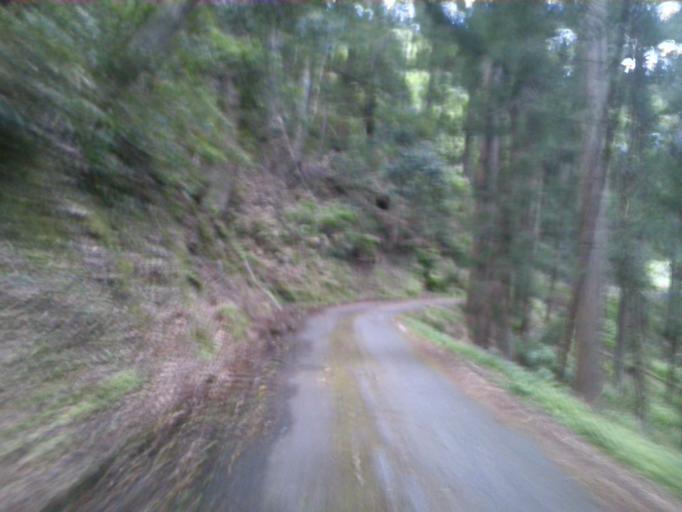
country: JP
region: Kyoto
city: Miyazu
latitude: 35.6617
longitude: 135.1263
